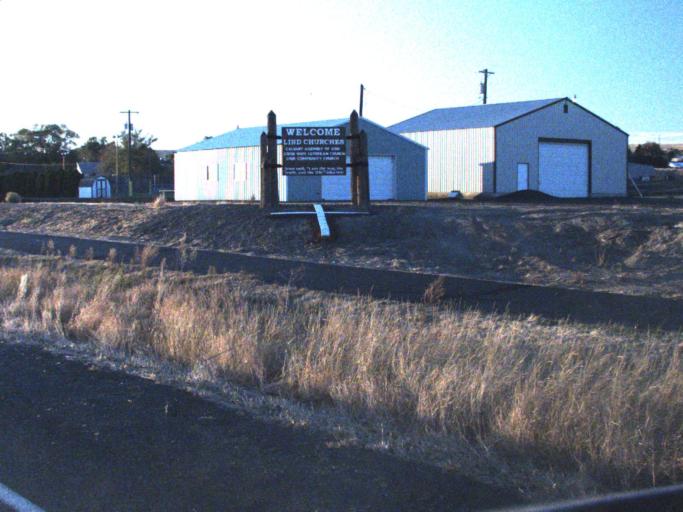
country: US
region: Washington
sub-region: Adams County
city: Ritzville
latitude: 46.9714
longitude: -118.6075
